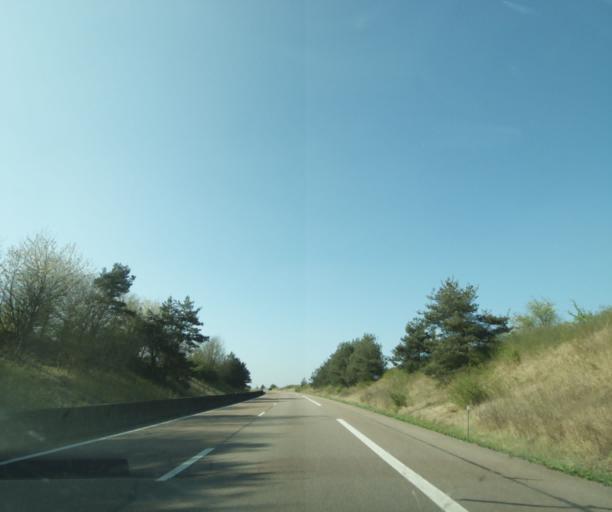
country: FR
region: Ile-de-France
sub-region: Departement de Seine-et-Marne
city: Souppes-sur-Loing
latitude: 48.2178
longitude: 2.7743
